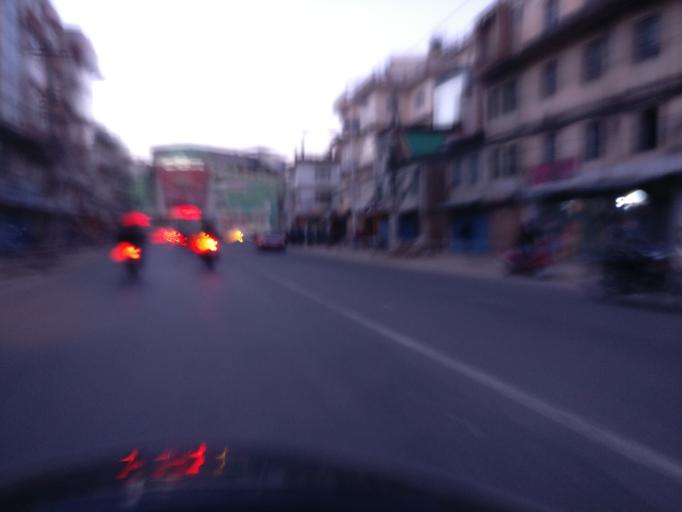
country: NP
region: Central Region
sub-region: Bagmati Zone
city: Kathmandu
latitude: 27.6930
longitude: 85.3149
